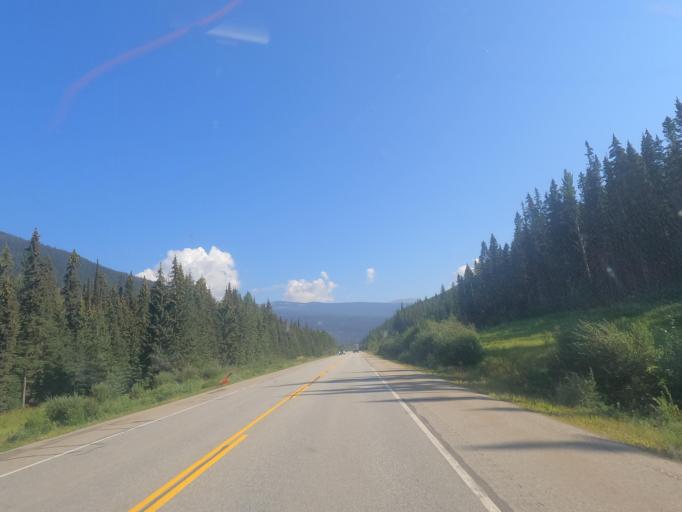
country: CA
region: Alberta
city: Jasper Park Lodge
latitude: 52.8707
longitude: -118.5037
